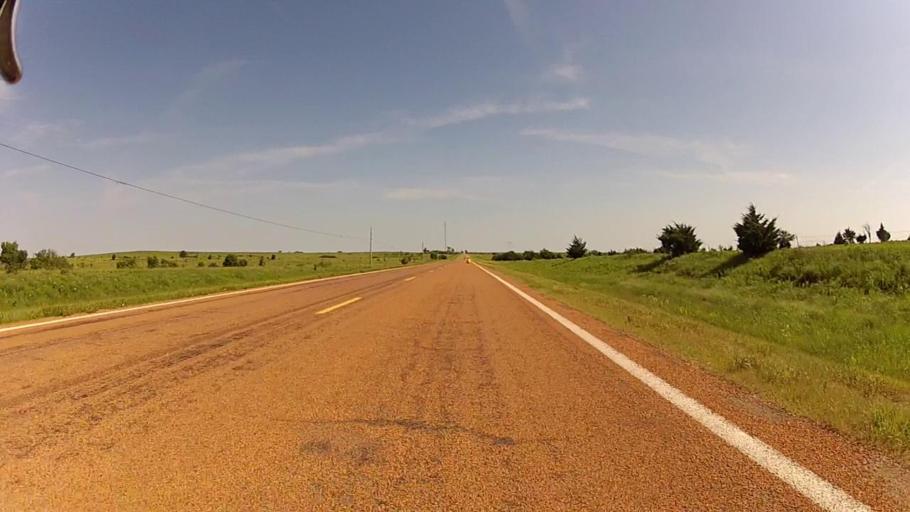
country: US
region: Kansas
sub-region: Cowley County
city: Winfield
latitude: 37.1008
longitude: -96.6436
